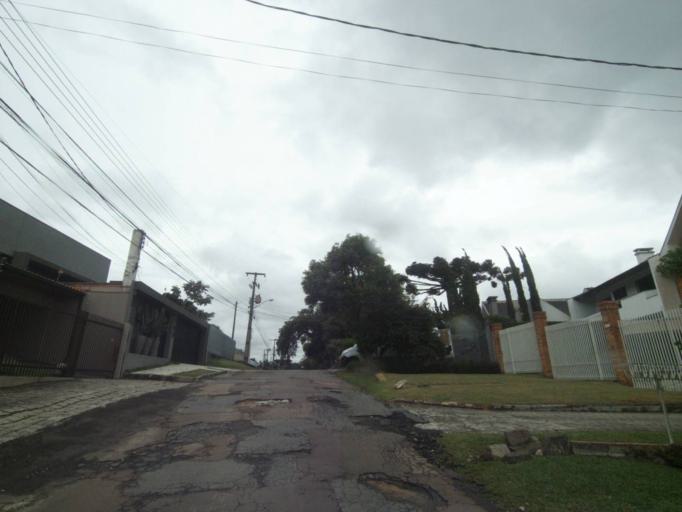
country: BR
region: Parana
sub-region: Curitiba
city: Curitiba
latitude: -25.4493
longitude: -49.3217
